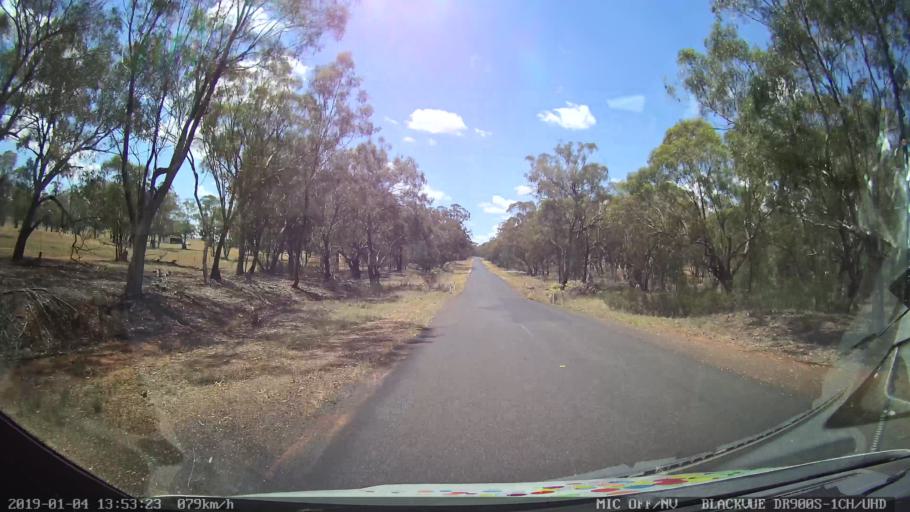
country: AU
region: New South Wales
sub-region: Dubbo Municipality
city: Dubbo
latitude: -32.3838
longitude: 148.5740
